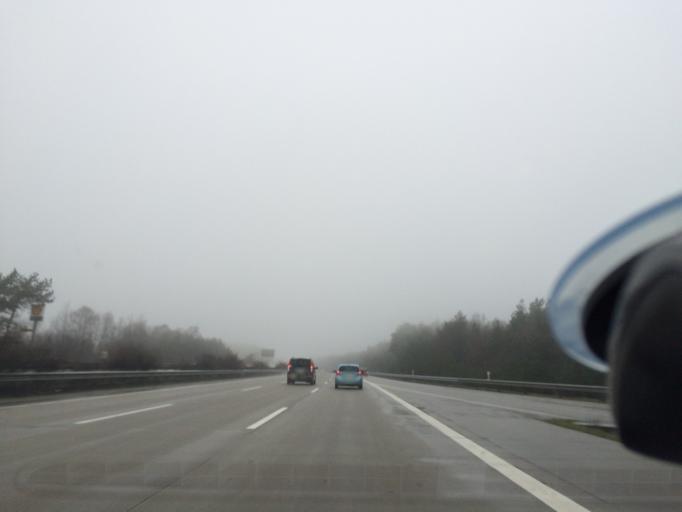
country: DE
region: Lower Saxony
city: Bispingen
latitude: 53.1122
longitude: 9.9848
